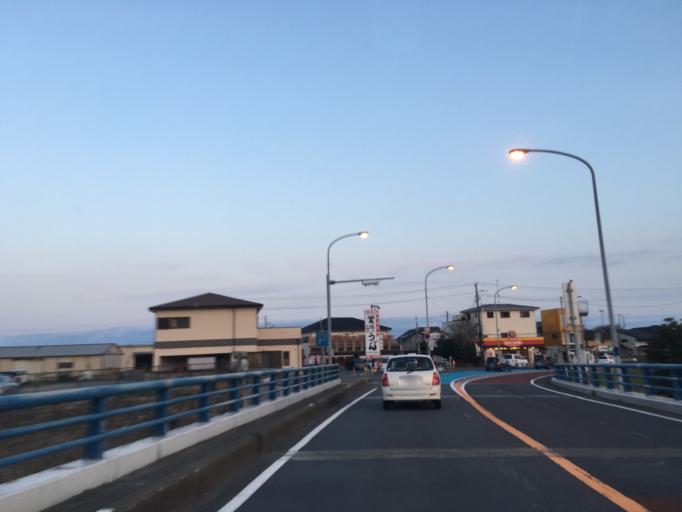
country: JP
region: Ibaraki
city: Kitaibaraki
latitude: 36.7892
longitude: 140.7489
